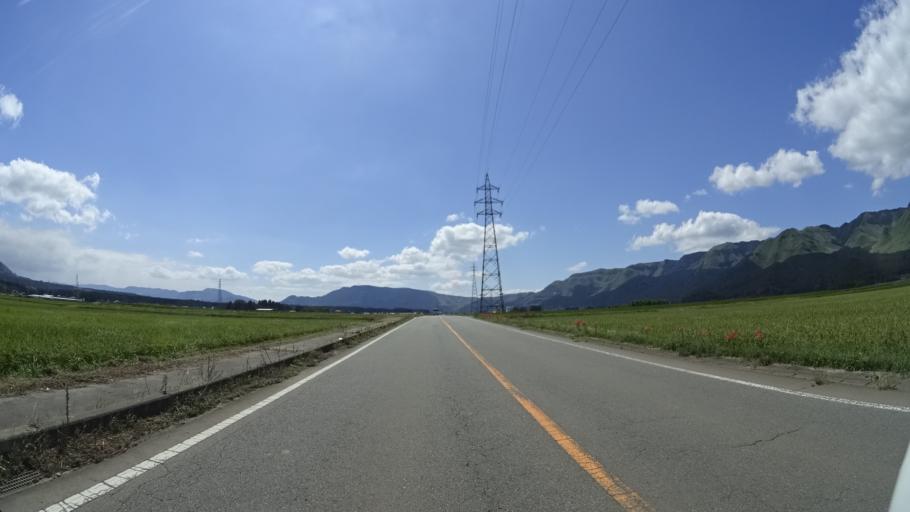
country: JP
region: Kumamoto
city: Aso
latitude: 32.9388
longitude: 131.0189
